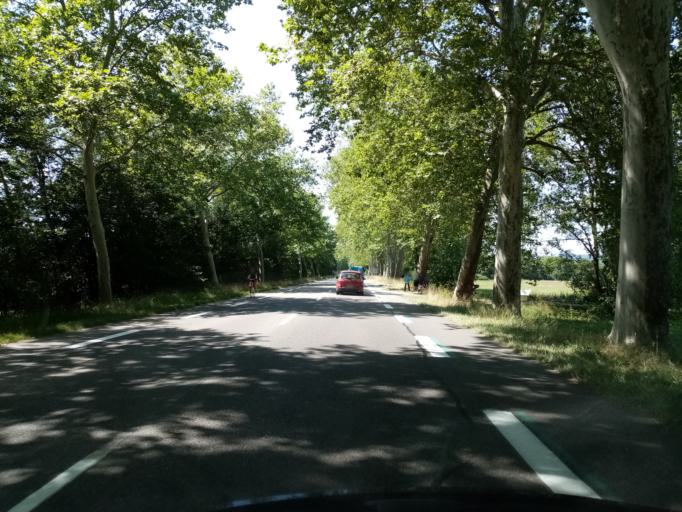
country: FR
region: Alsace
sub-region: Departement du Bas-Rhin
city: Selestat
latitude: 48.2440
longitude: 7.4664
